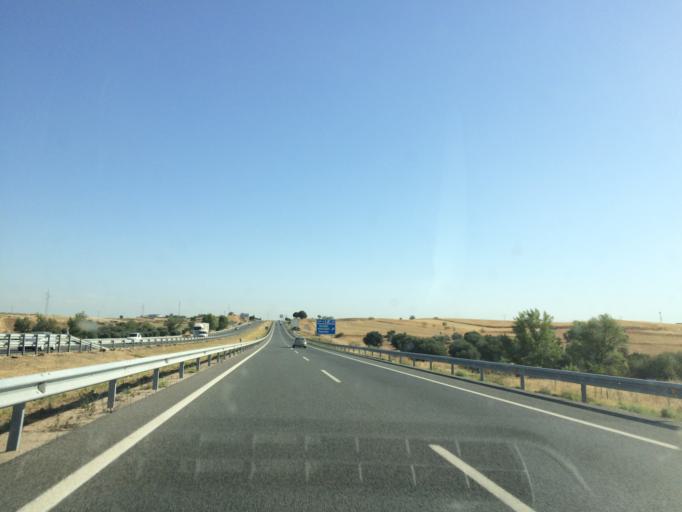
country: ES
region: Castille-La Mancha
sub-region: Province of Toledo
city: Valmojado
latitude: 40.1979
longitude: -4.1060
